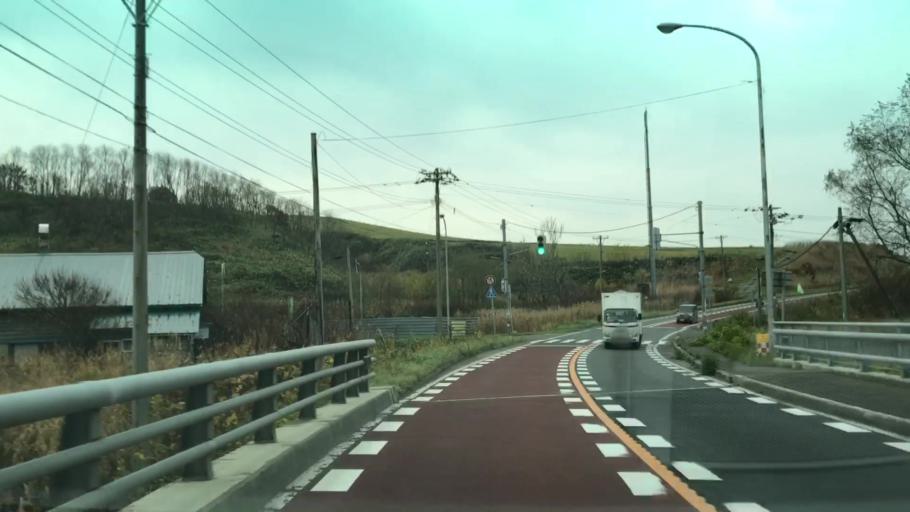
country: JP
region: Hokkaido
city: Ishikari
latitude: 43.3556
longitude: 141.4303
